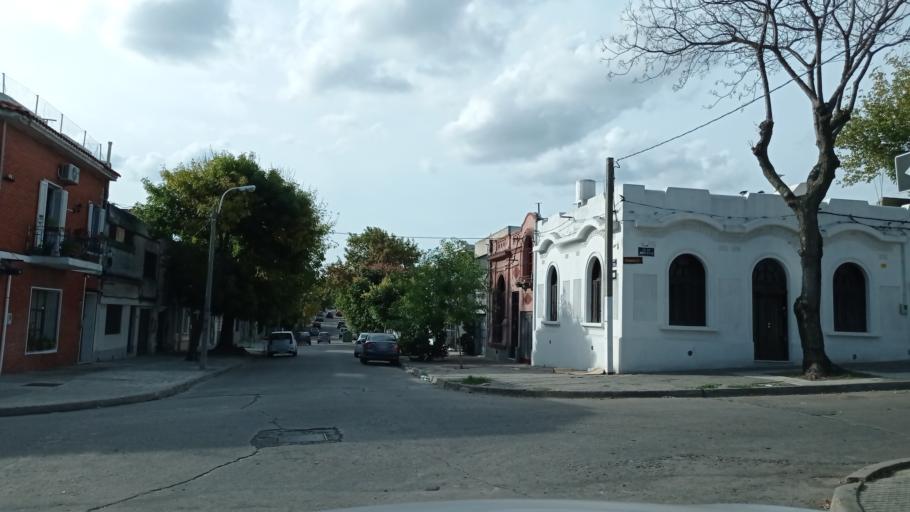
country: UY
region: Montevideo
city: Montevideo
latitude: -34.8878
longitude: -56.1748
